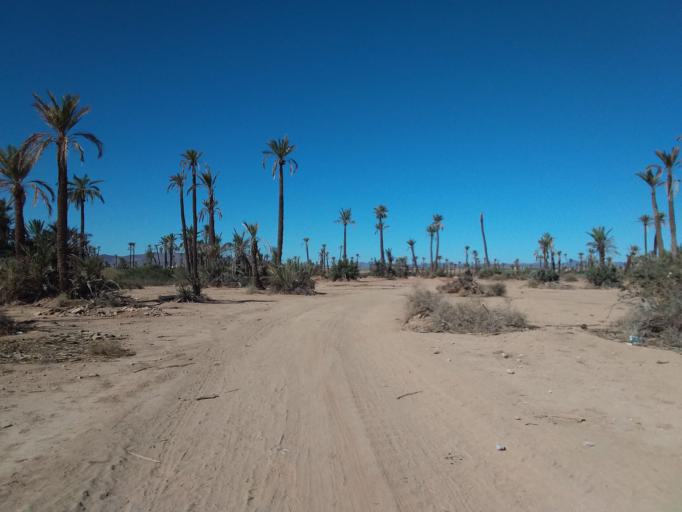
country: MA
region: Marrakech-Tensift-Al Haouz
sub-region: Marrakech
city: Marrakesh
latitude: 31.6794
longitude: -7.9518
